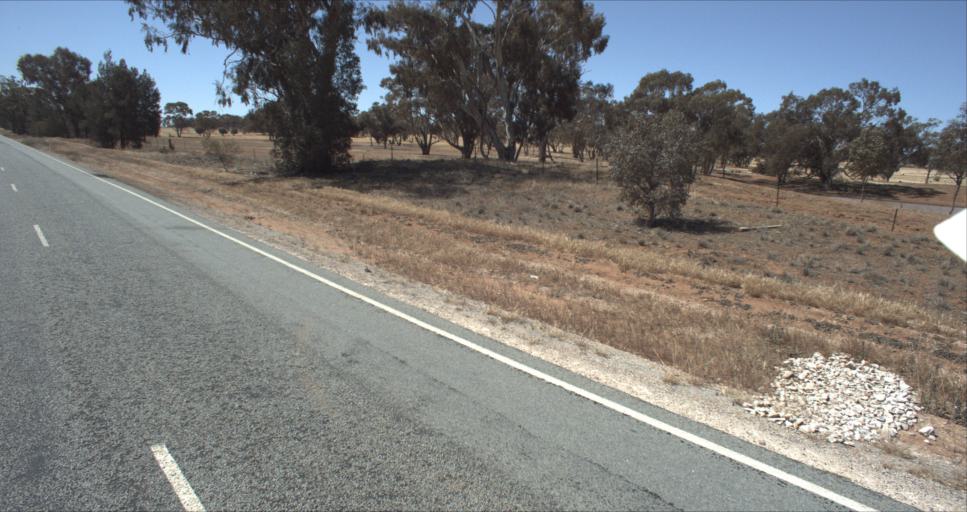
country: AU
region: New South Wales
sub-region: Leeton
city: Leeton
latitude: -34.4837
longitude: 146.4337
